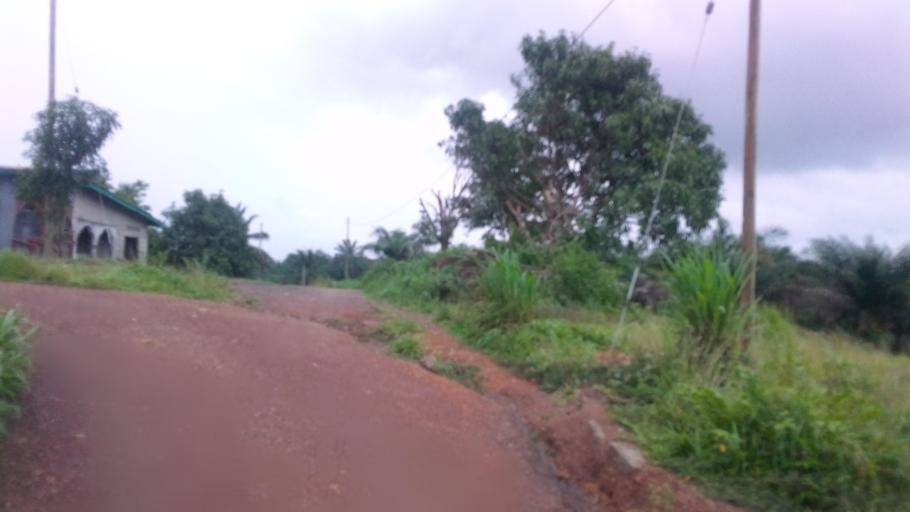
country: SL
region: Eastern Province
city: Kenema
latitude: 7.8842
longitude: -11.1627
